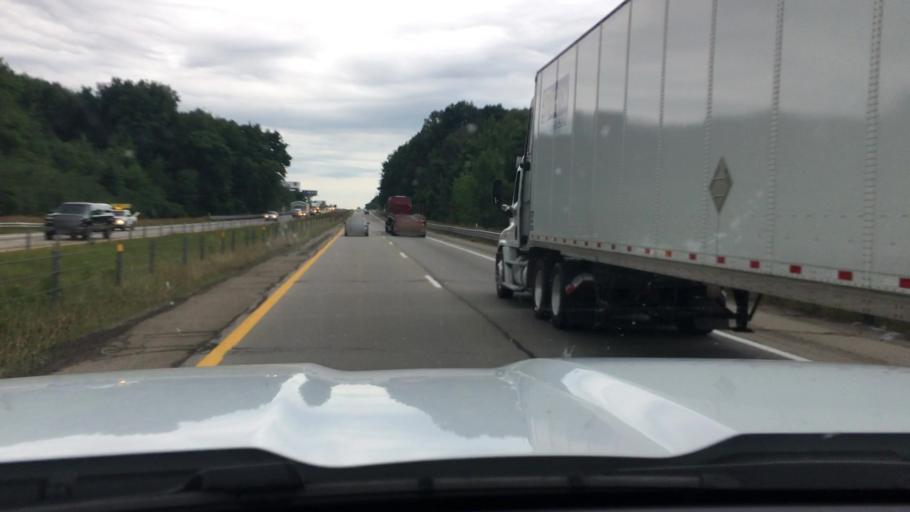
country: US
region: Michigan
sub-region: Kent County
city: Byron Center
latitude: 42.7769
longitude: -85.6698
